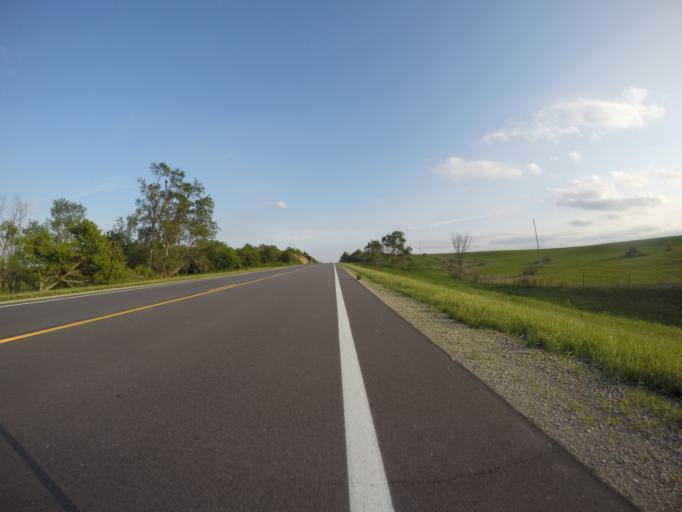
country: US
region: Kansas
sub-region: Pottawatomie County
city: Westmoreland
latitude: 39.4119
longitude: -96.5200
